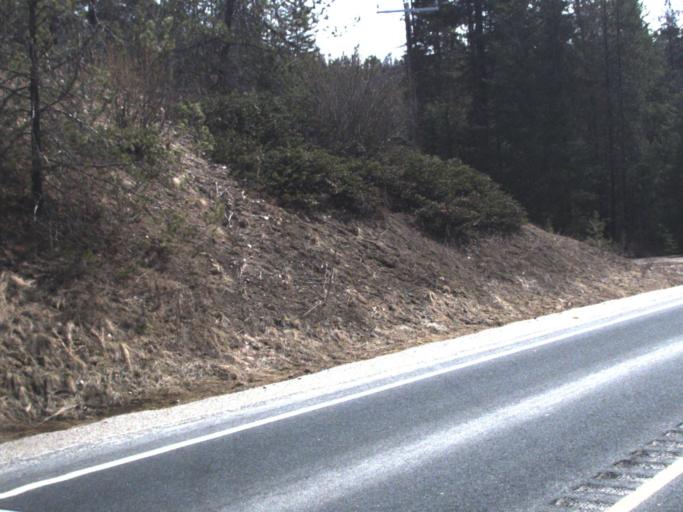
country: US
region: Washington
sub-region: Stevens County
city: Colville
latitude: 48.5126
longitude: -117.6804
